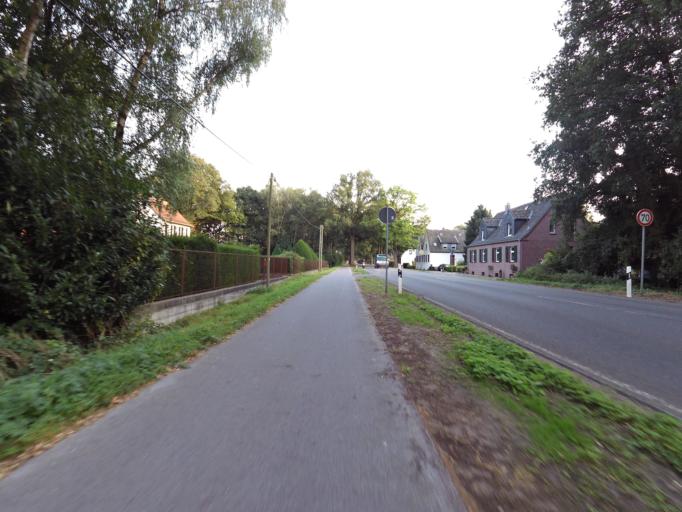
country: NL
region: Gelderland
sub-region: Gemeente Zevenaar
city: Zevenaar
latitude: 51.8868
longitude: 6.1512
